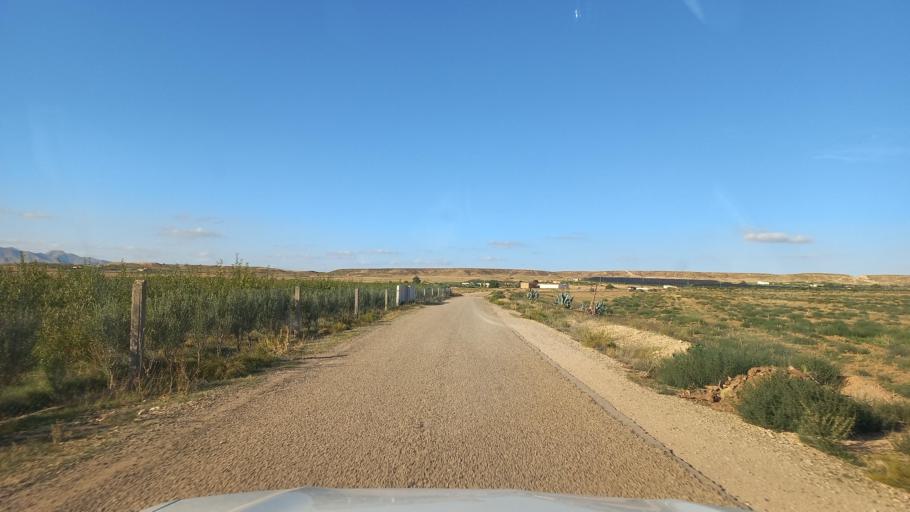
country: TN
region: Al Qasrayn
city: Sbiba
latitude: 35.3384
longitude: 9.1191
